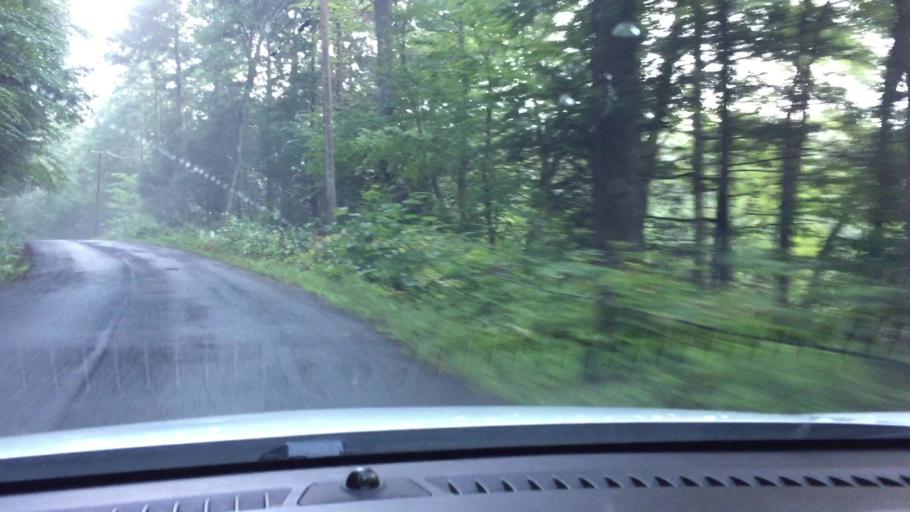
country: US
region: Massachusetts
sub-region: Hampshire County
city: Chesterfield
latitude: 42.3314
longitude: -72.9336
